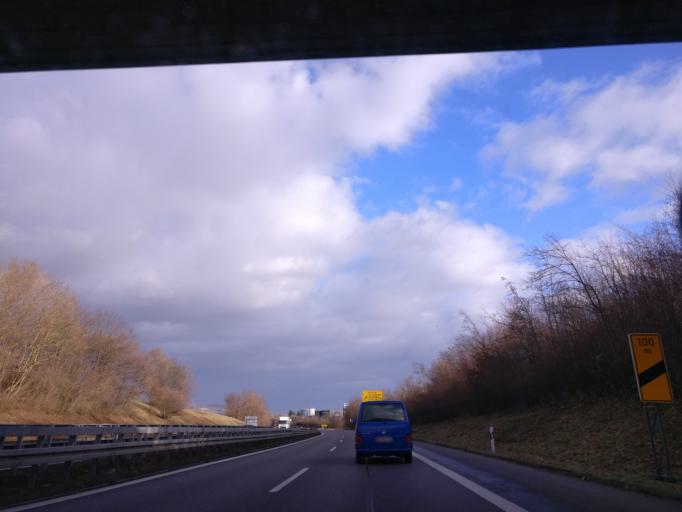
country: DE
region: Baden-Wuerttemberg
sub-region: Regierungsbezirk Stuttgart
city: Weinstadt-Endersbach
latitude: 48.8140
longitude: 9.3447
